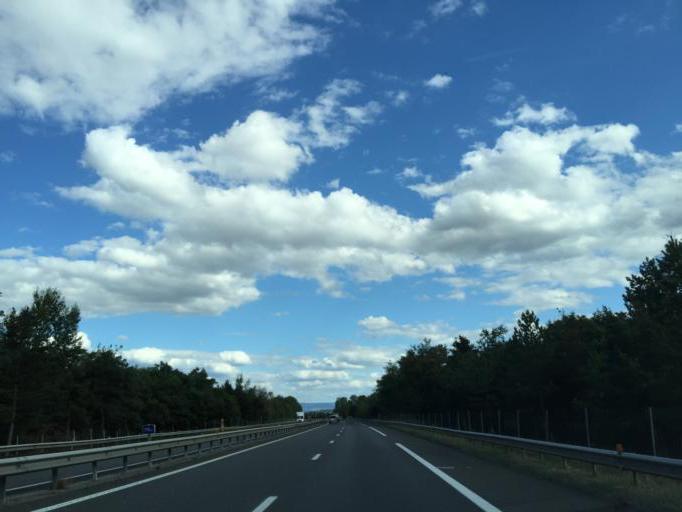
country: FR
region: Rhone-Alpes
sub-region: Departement de la Loire
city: Saint-Cyprien
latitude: 45.5720
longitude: 4.2216
